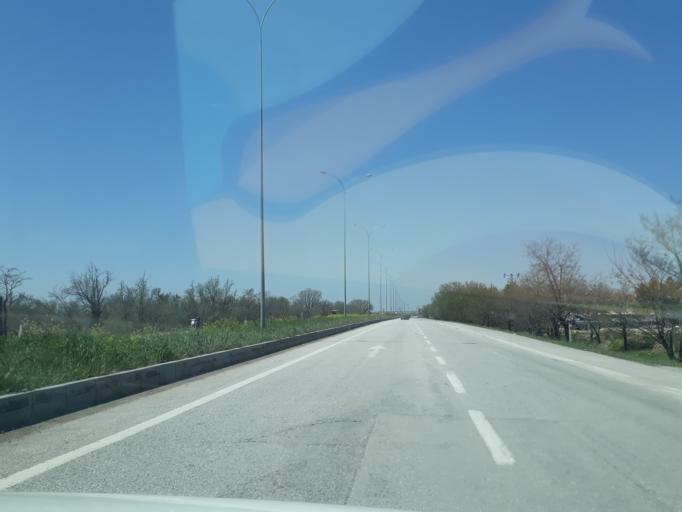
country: TR
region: Konya
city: Karapinar
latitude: 37.7144
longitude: 33.5219
